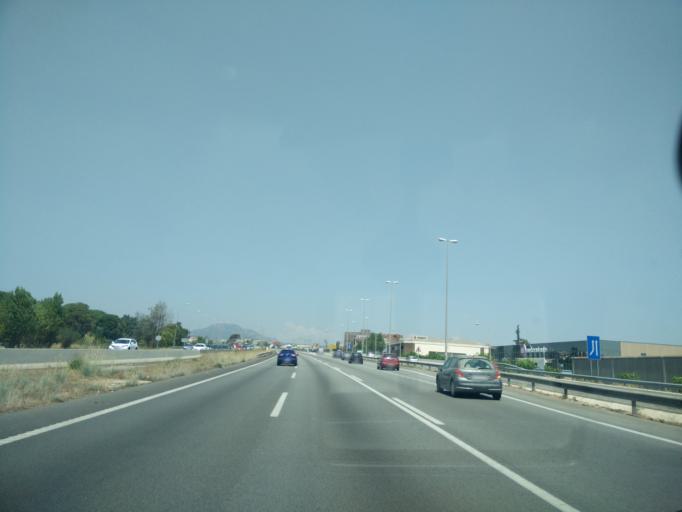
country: ES
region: Catalonia
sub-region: Provincia de Barcelona
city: Sant Quirze del Valles
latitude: 41.5249
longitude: 2.0962
